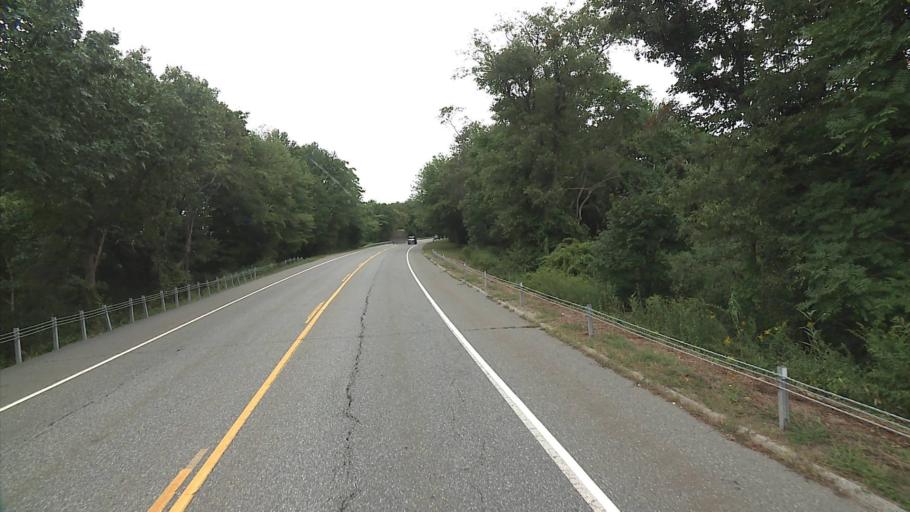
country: US
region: Connecticut
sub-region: Middlesex County
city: Old Saybrook Center
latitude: 41.3112
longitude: -72.3353
